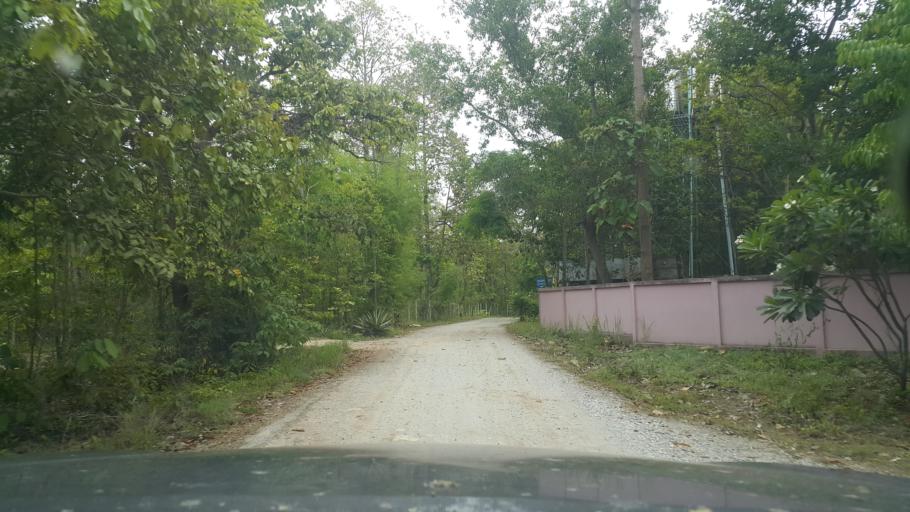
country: TH
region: Chiang Mai
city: San Pa Tong
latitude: 18.6502
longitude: 98.8504
